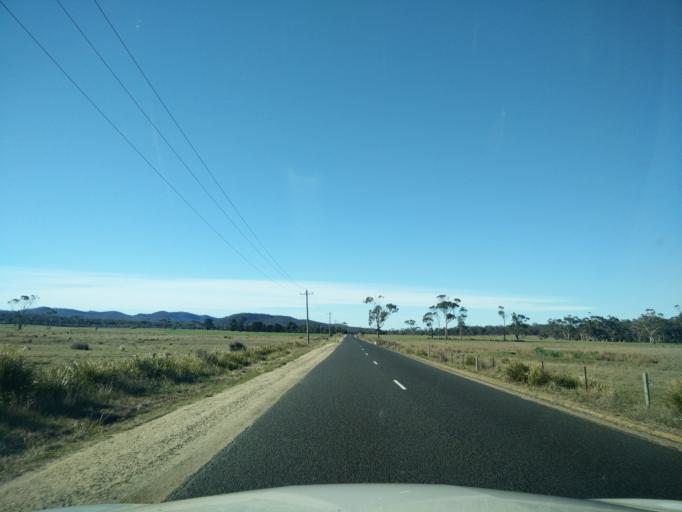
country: AU
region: Tasmania
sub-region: Break O'Day
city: St Helens
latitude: -41.9025
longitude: 148.2543
